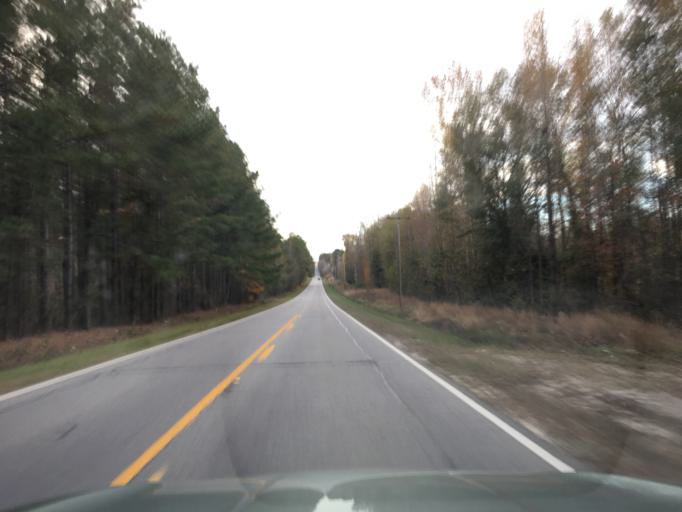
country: US
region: South Carolina
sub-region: Lexington County
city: Leesville
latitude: 33.7969
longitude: -81.4274
